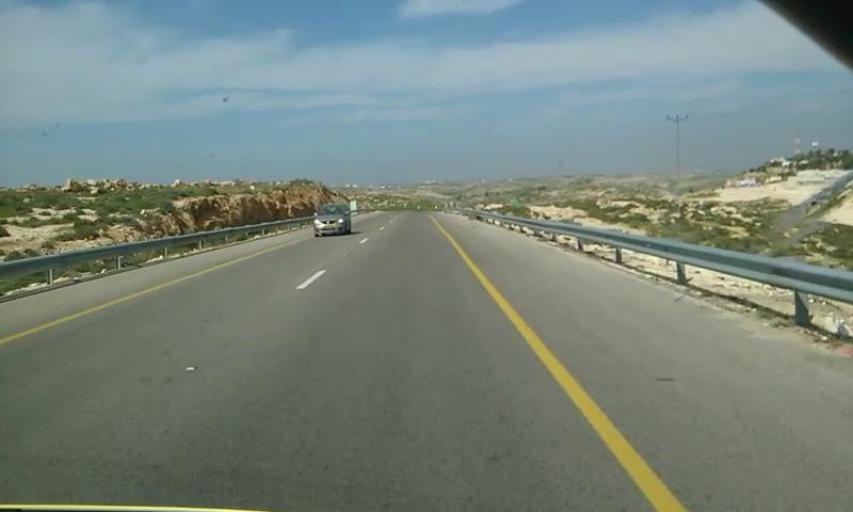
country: PS
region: West Bank
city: Az Zahiriyah
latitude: 31.3824
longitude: 35.0050
